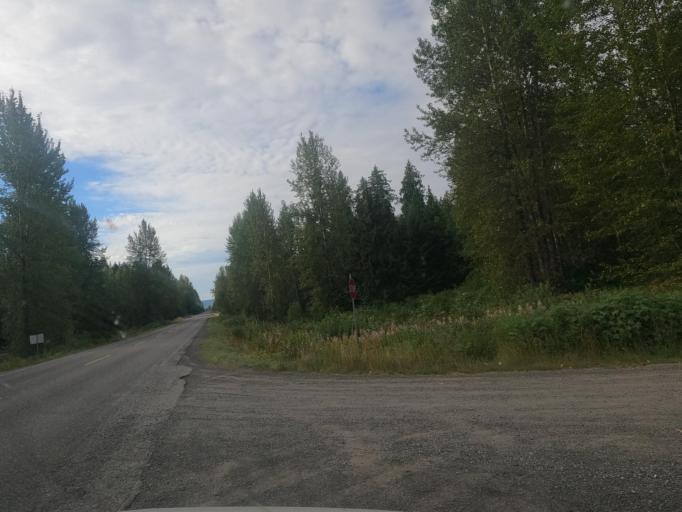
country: CA
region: British Columbia
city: Terrace
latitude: 55.3255
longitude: -128.0901
